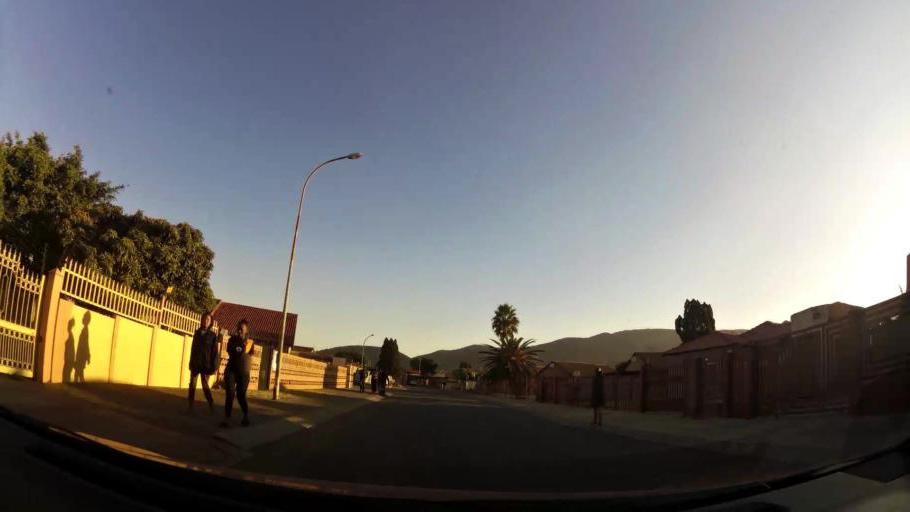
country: ZA
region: North-West
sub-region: Bojanala Platinum District Municipality
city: Rustenburg
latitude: -25.6427
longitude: 27.2104
